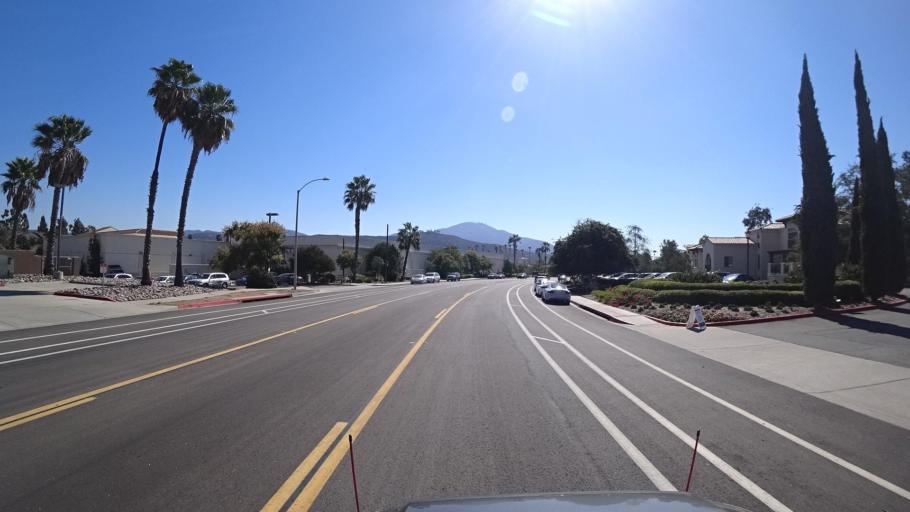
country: US
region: California
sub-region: San Diego County
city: Rancho San Diego
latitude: 32.7482
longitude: -116.9294
